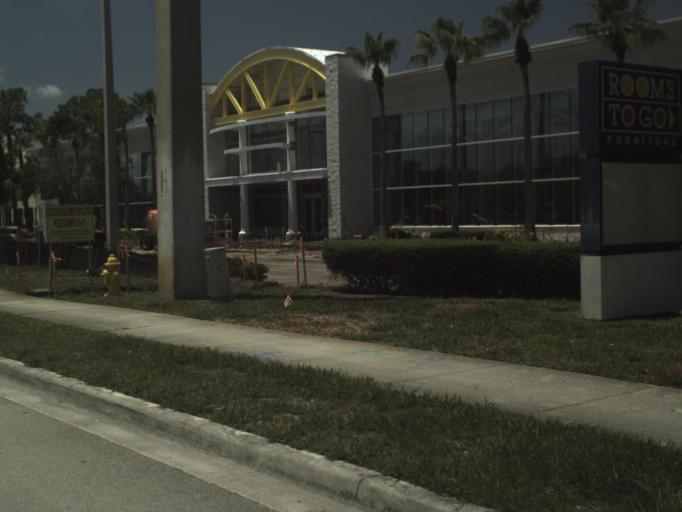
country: US
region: Florida
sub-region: Martin County
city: North River Shores
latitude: 27.2422
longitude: -80.2712
